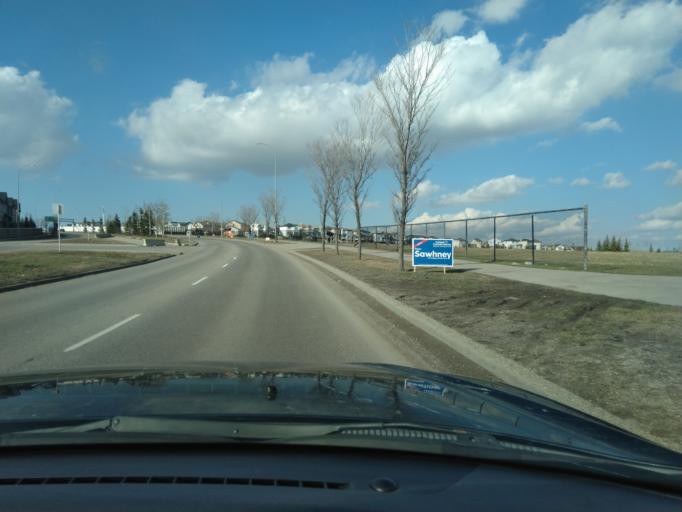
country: CA
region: Alberta
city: Calgary
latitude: 51.1662
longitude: -114.0685
